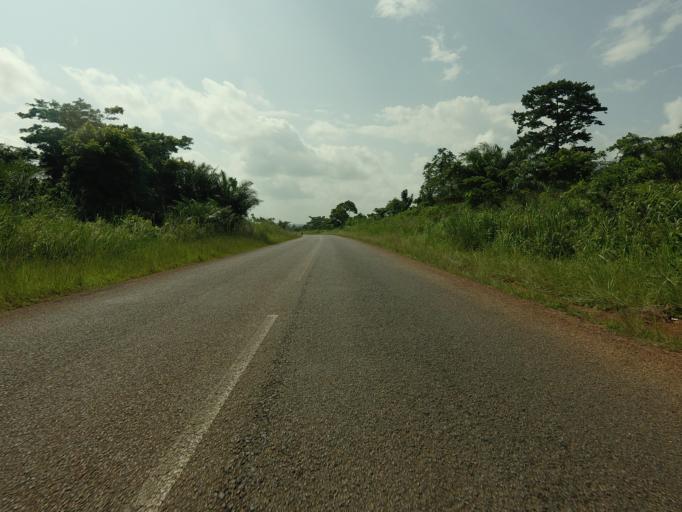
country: TG
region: Maritime
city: Tsevie
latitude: 6.3526
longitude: 0.8705
